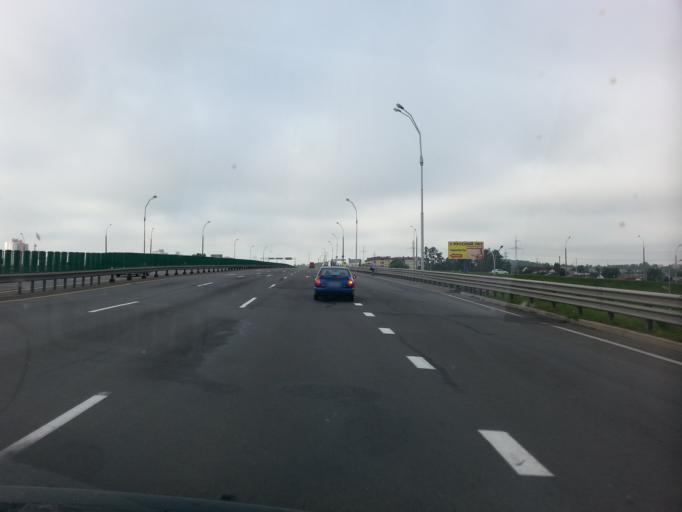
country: BY
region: Minsk
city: Zhdanovichy
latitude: 53.9446
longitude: 27.4371
